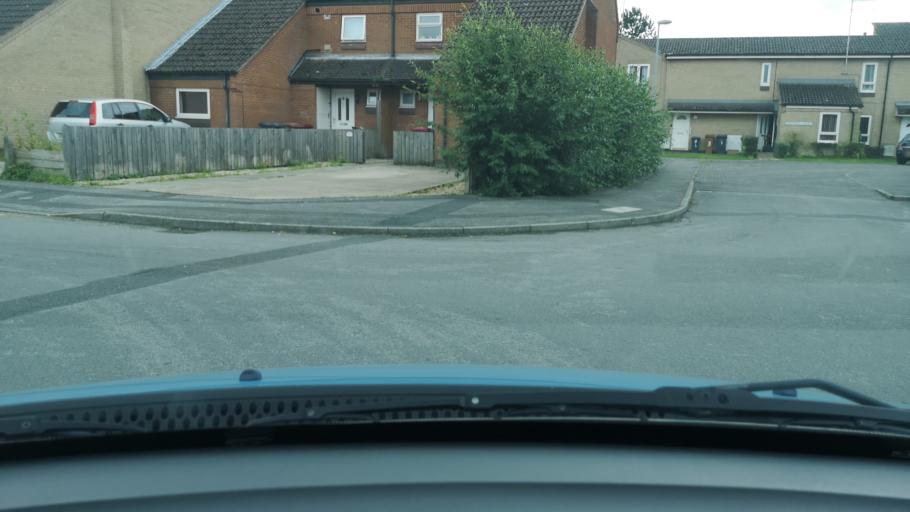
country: GB
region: England
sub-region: North Lincolnshire
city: Scunthorpe
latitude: 53.5881
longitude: -0.6906
